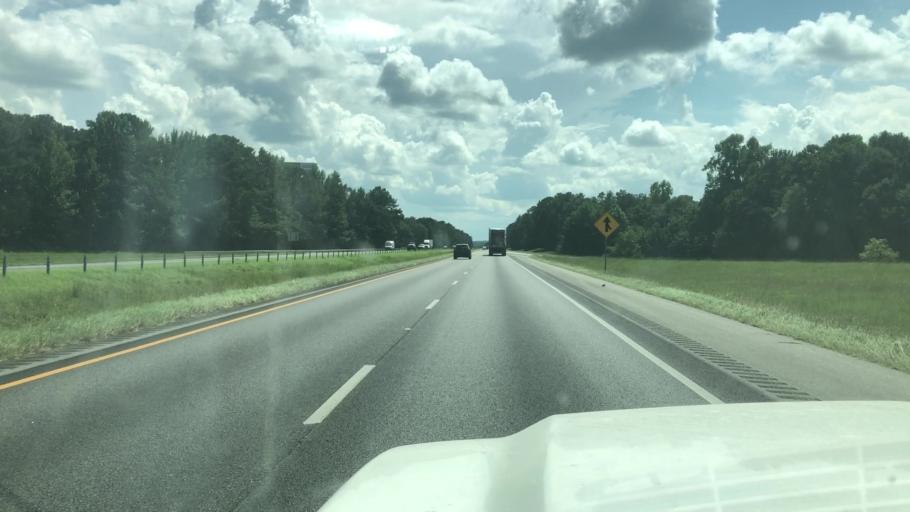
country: US
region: Alabama
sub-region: Lee County
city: Opelika
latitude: 32.6718
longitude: -85.3326
